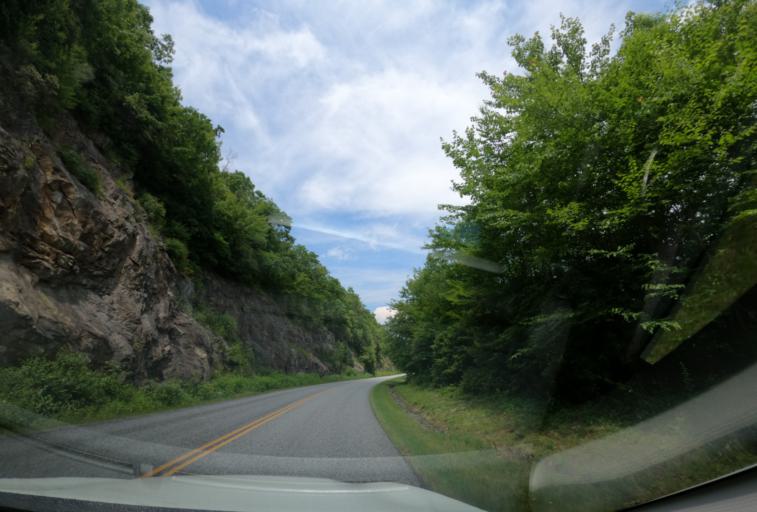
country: US
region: North Carolina
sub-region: Haywood County
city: Canton
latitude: 35.4250
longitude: -82.7408
